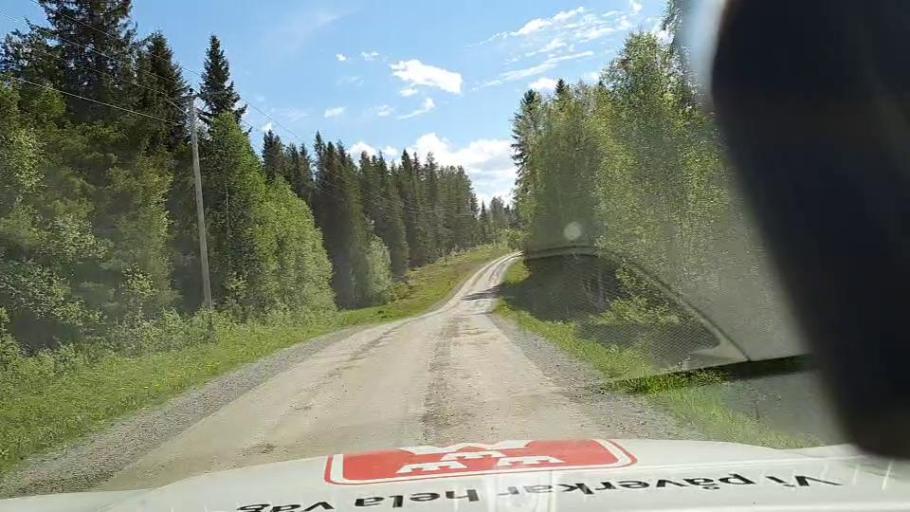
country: SE
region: Jaemtland
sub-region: Stroemsunds Kommun
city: Stroemsund
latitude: 64.4663
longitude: 15.5949
